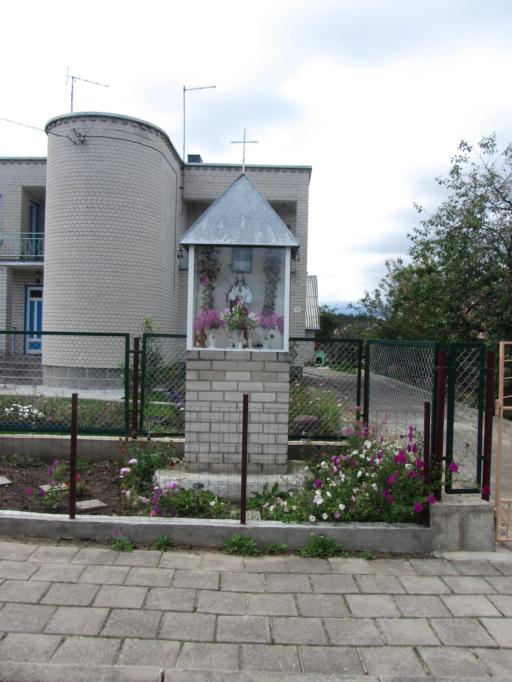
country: LT
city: Salcininkai
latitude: 54.2995
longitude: 25.3838
